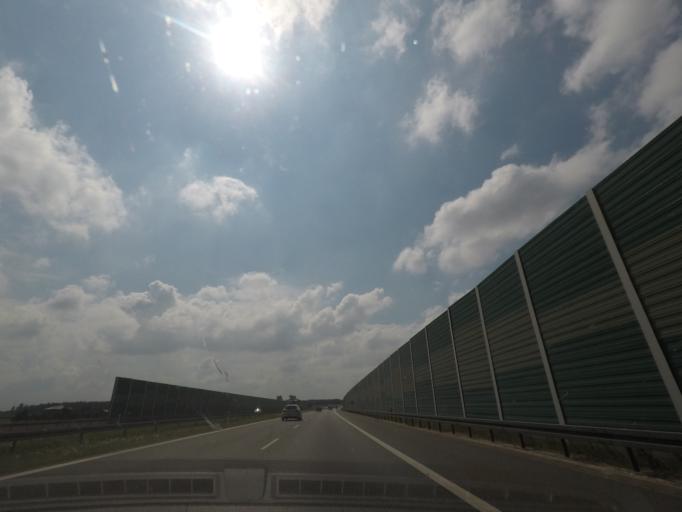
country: PL
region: Lodz Voivodeship
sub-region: Powiat kutnowski
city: Krzyzanow
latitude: 52.2050
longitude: 19.4834
